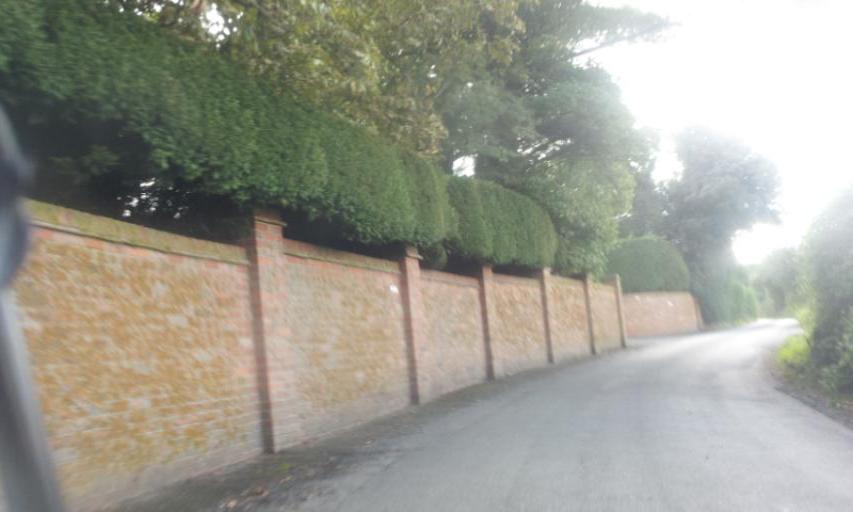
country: GB
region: England
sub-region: Kent
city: Newington
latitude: 51.3405
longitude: 0.6474
